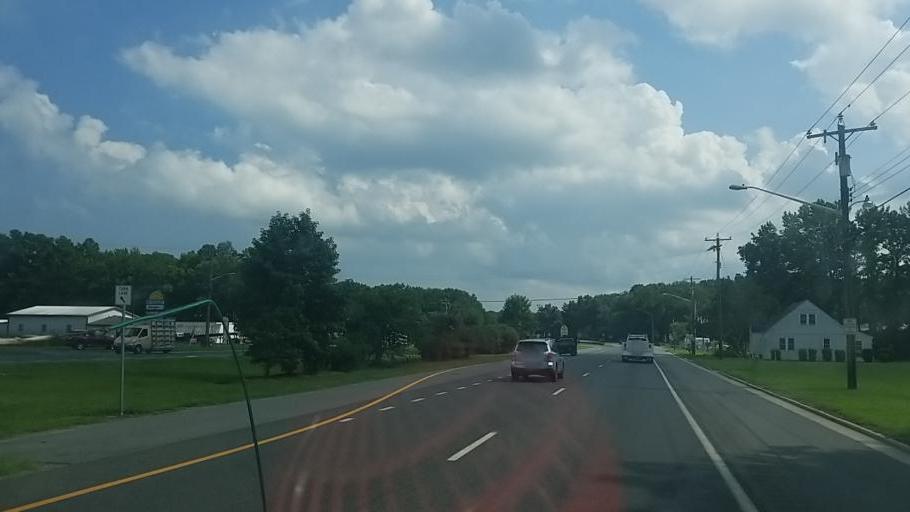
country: US
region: Delaware
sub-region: Sussex County
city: Selbyville
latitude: 38.4532
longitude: -75.2333
